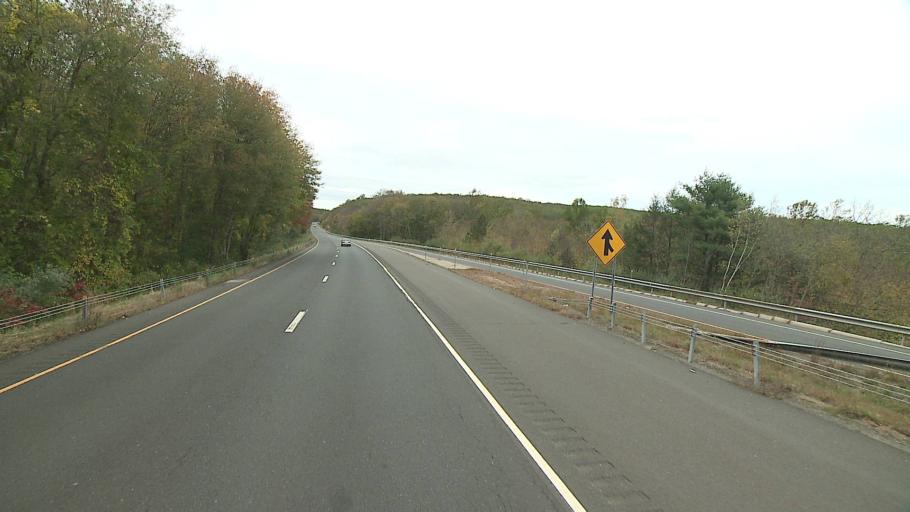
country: US
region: Connecticut
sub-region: Middlesex County
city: Chester Center
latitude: 41.4209
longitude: -72.4951
